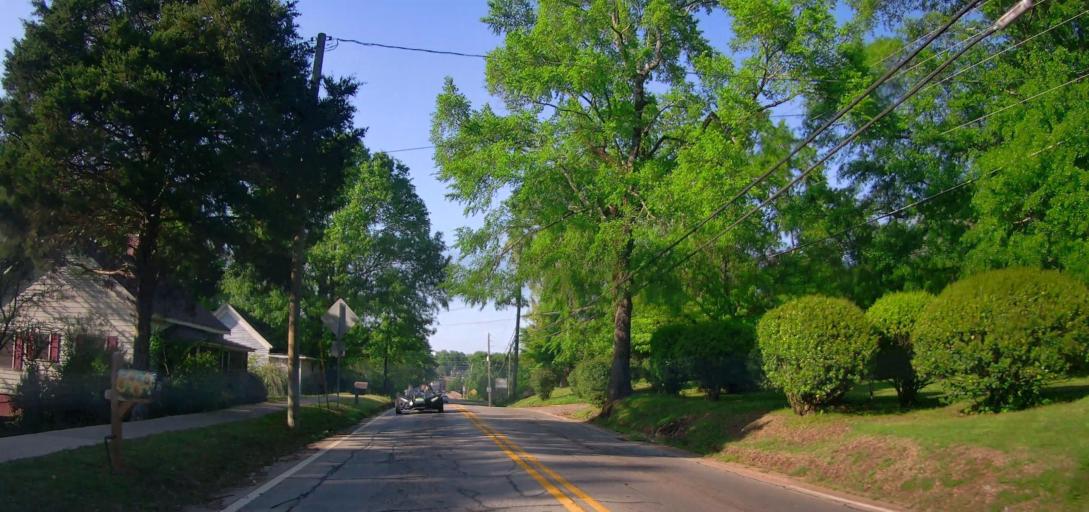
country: US
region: Georgia
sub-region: Newton County
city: Porterdale
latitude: 33.5684
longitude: -83.8978
